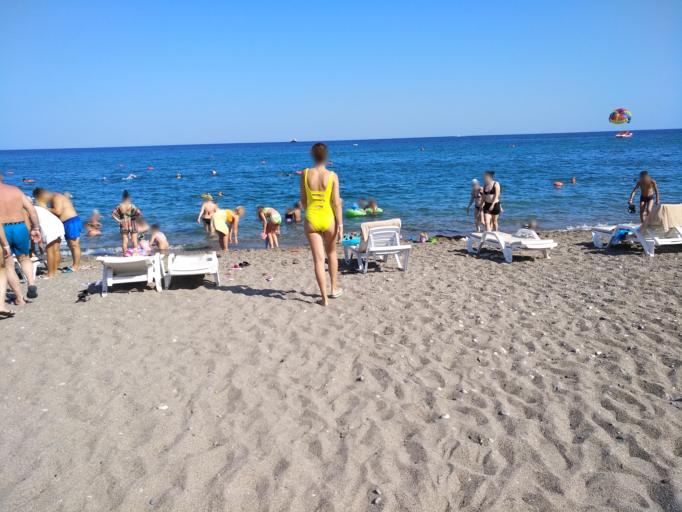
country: TR
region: Antalya
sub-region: Kemer
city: Goeynuek
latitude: 36.6652
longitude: 30.5637
